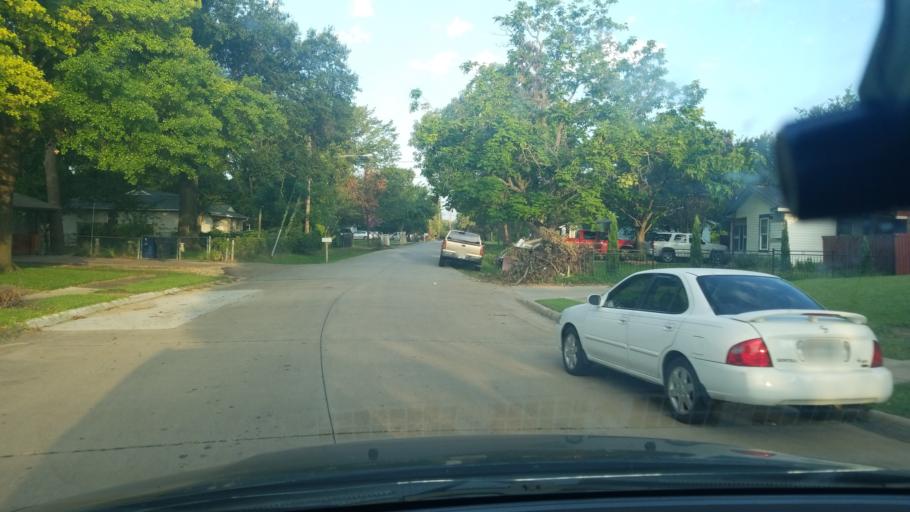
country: US
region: Texas
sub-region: Dallas County
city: Balch Springs
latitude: 32.7290
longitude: -96.6533
